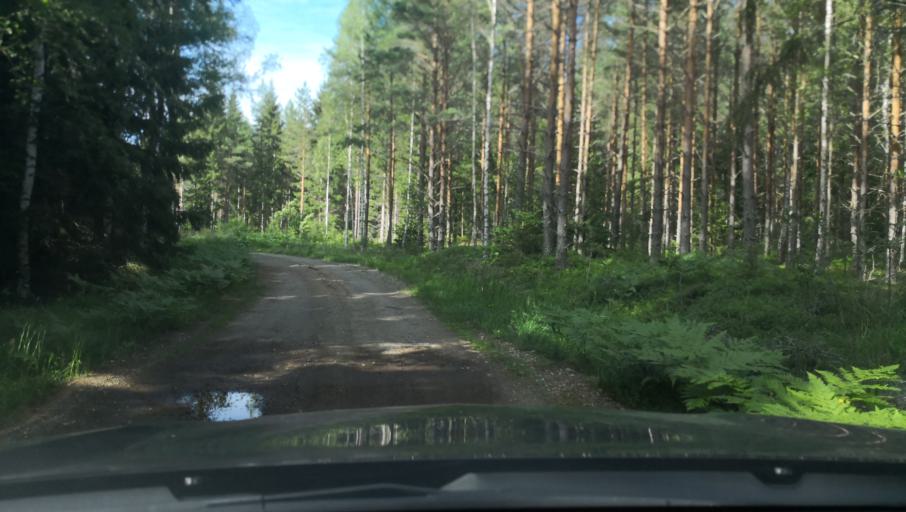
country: SE
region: Vaestmanland
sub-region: Surahammars Kommun
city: Surahammar
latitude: 59.6712
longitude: 16.1087
